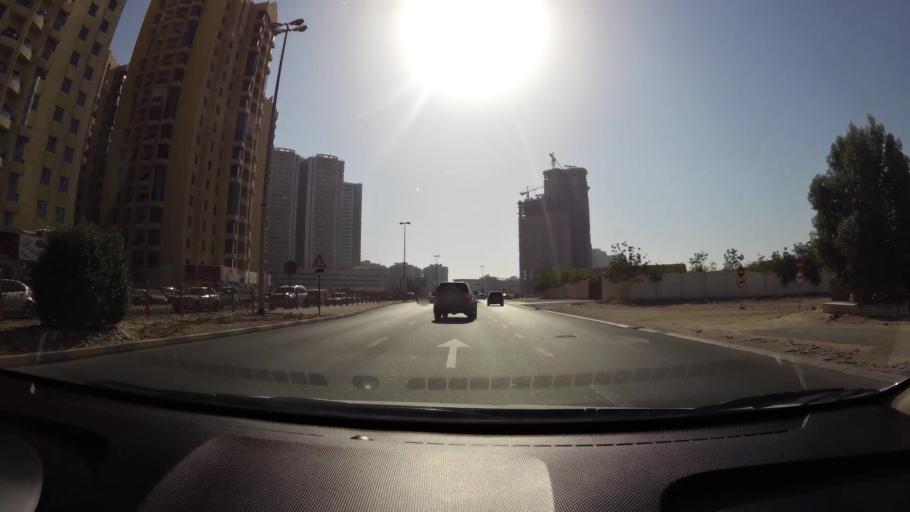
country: AE
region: Ajman
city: Ajman
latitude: 25.3953
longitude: 55.4585
